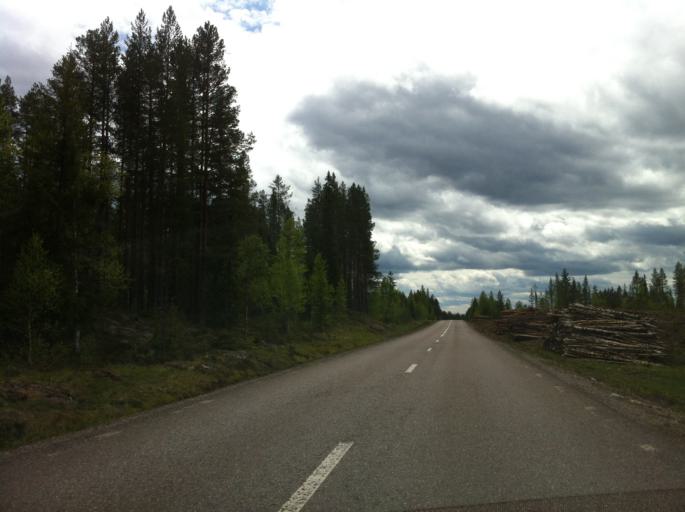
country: NO
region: Hedmark
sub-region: Trysil
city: Innbygda
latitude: 61.5380
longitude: 13.0830
